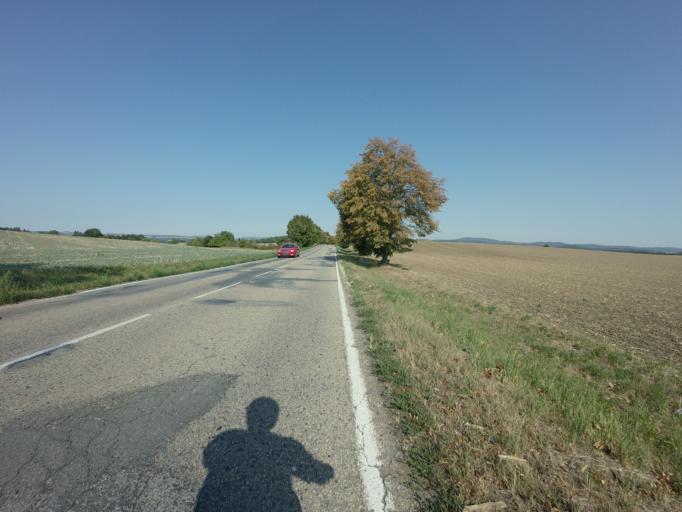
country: CZ
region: Central Bohemia
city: Porici nad Sazavou
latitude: 49.8170
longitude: 14.6387
